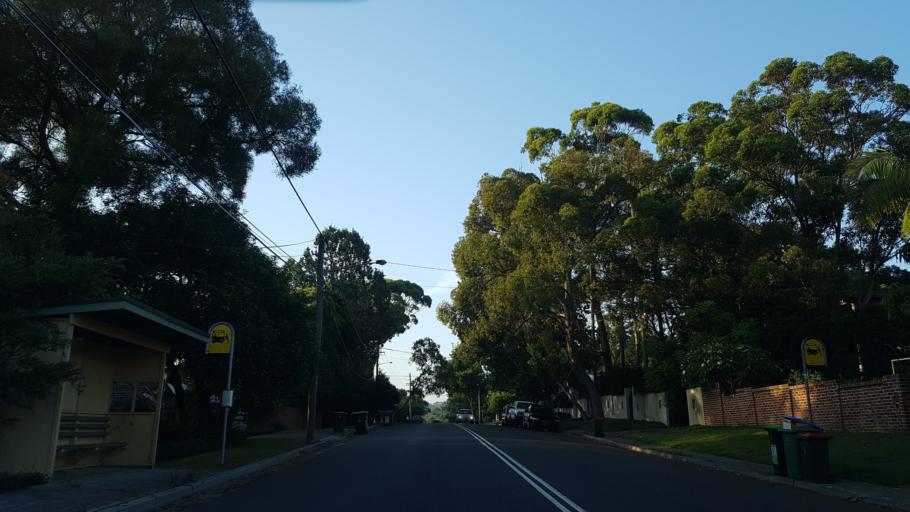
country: AU
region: New South Wales
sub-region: Warringah
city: Narraweena
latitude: -33.7321
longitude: 151.2733
